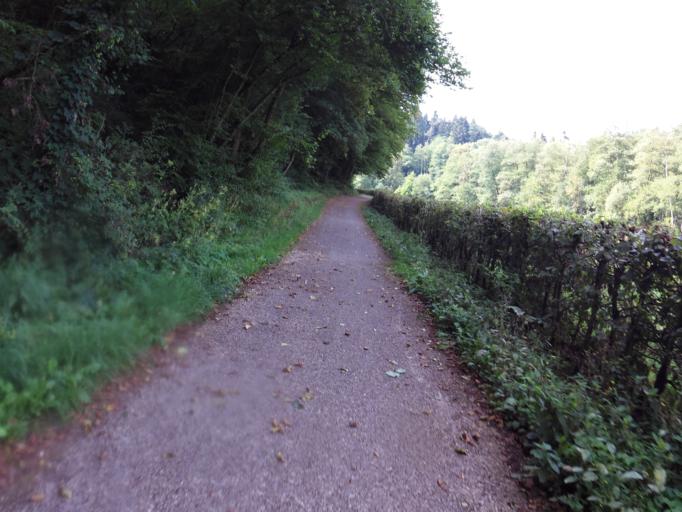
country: DE
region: Rheinland-Pfalz
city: Philippsheim
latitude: 49.9497
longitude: 6.6280
